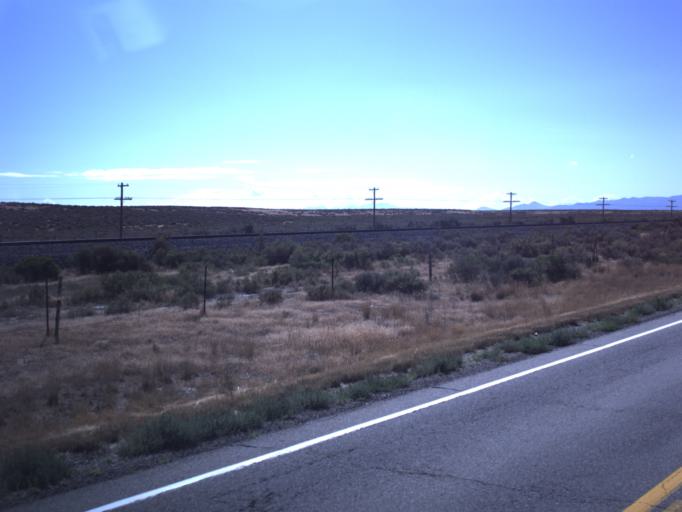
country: US
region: Utah
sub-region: Tooele County
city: Tooele
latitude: 40.3499
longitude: -112.4121
